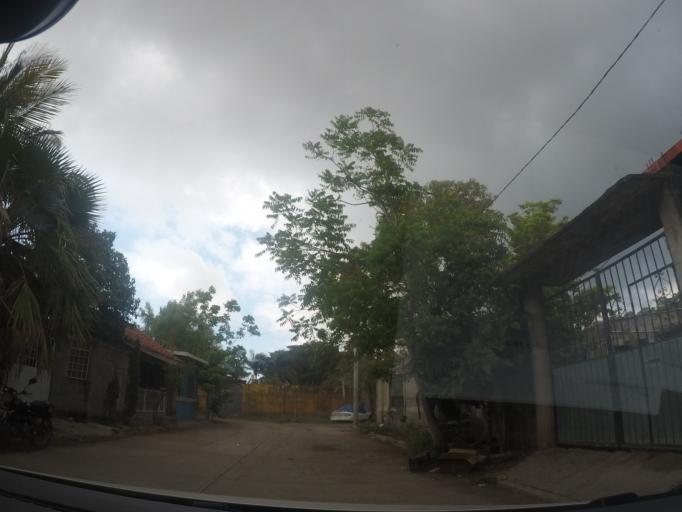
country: MX
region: Oaxaca
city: Juchitan de Zaragoza
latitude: 16.4310
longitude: -95.0324
